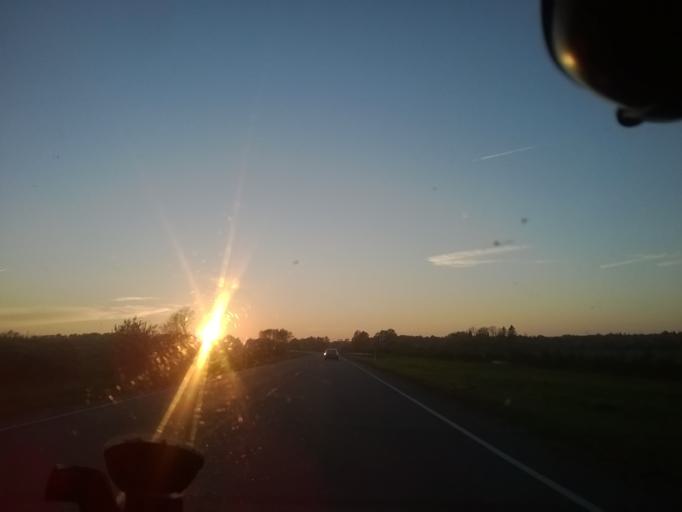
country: EE
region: Laeaene
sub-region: Ridala Parish
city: Uuemoisa
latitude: 58.9577
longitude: 23.7937
